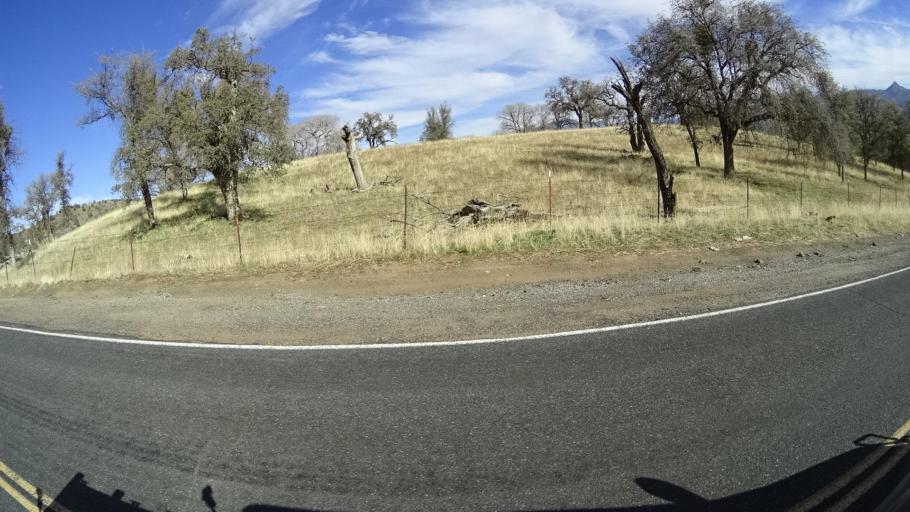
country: US
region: California
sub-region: Kern County
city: Alta Sierra
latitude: 35.6610
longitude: -118.7493
